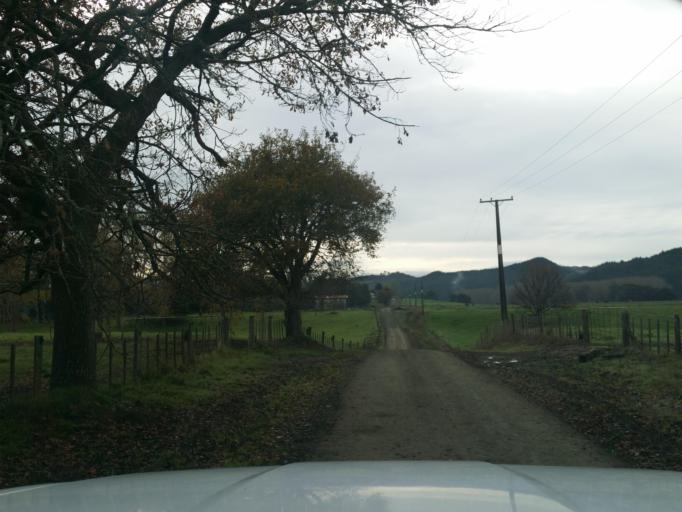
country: NZ
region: Northland
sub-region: Whangarei
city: Maungatapere
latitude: -35.7994
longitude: 174.0528
